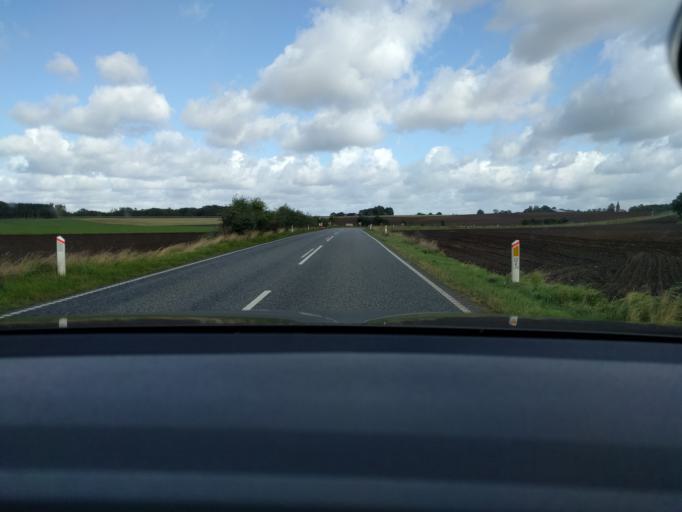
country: DK
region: Central Jutland
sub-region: Viborg Kommune
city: Bjerringbro
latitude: 56.3037
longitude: 9.6989
